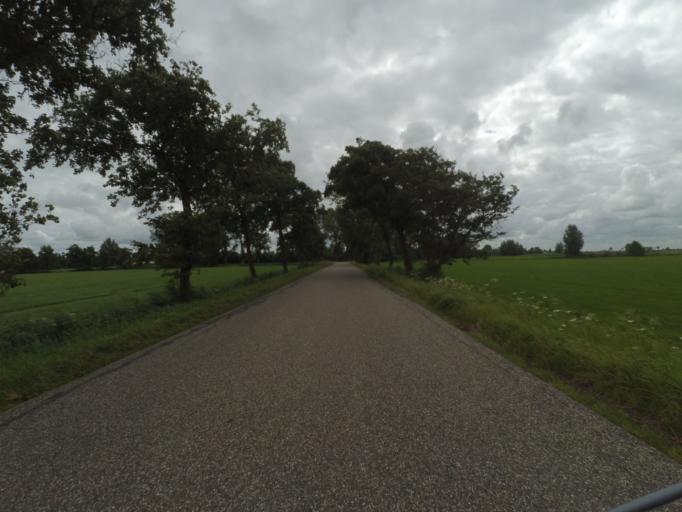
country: NL
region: Friesland
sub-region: Gemeente Kollumerland en Nieuwkruisland
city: Kollumerzwaag
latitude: 53.2963
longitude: 6.0831
